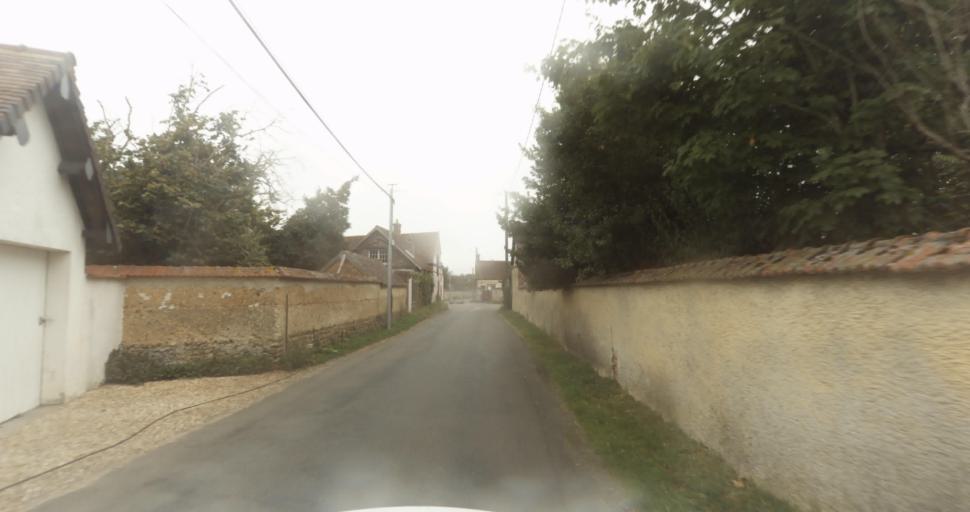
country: FR
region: Haute-Normandie
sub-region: Departement de l'Eure
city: Saint-Germain-sur-Avre
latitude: 48.7762
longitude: 1.2620
